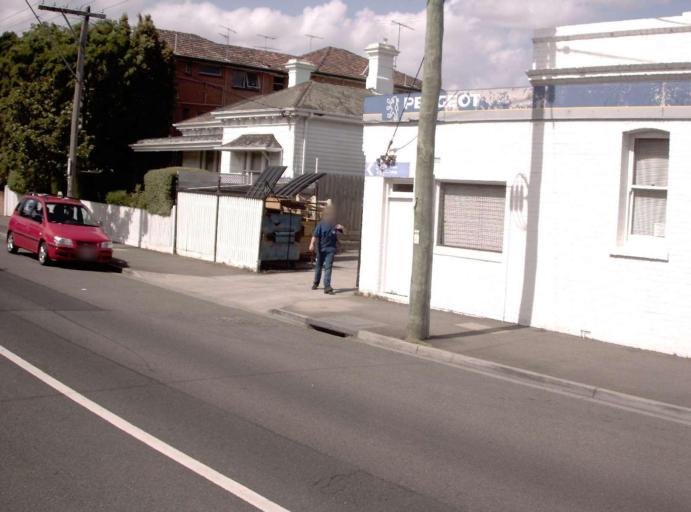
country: AU
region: Victoria
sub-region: Boroondara
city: Hawthorn East
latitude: -37.8214
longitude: 145.0452
